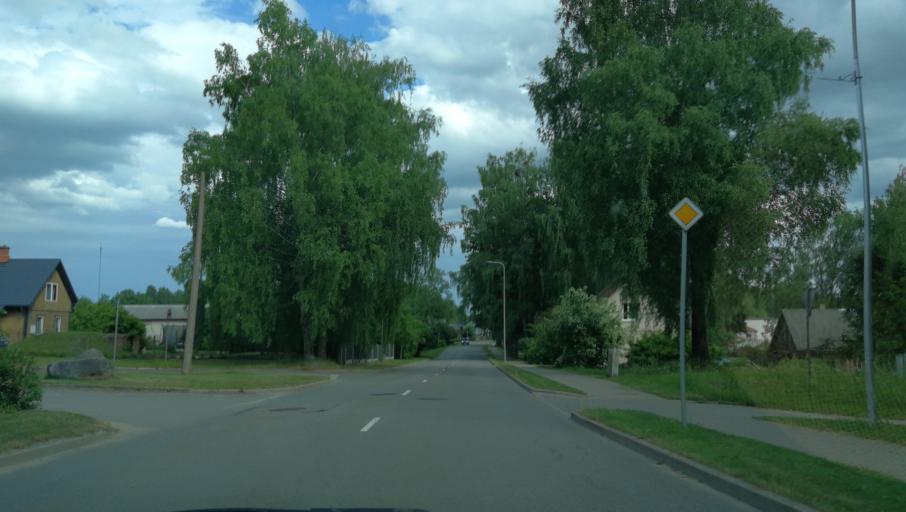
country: LV
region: Rujienas
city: Rujiena
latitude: 57.8962
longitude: 25.3339
